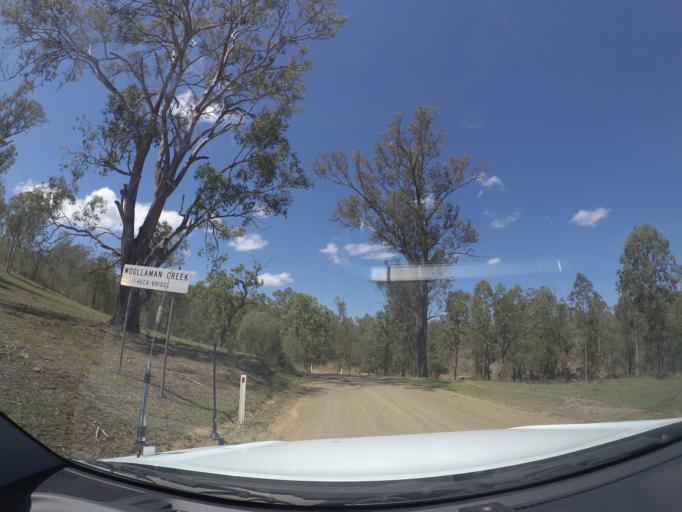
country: AU
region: Queensland
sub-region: Logan
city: Cedar Vale
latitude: -27.8584
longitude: 152.8613
